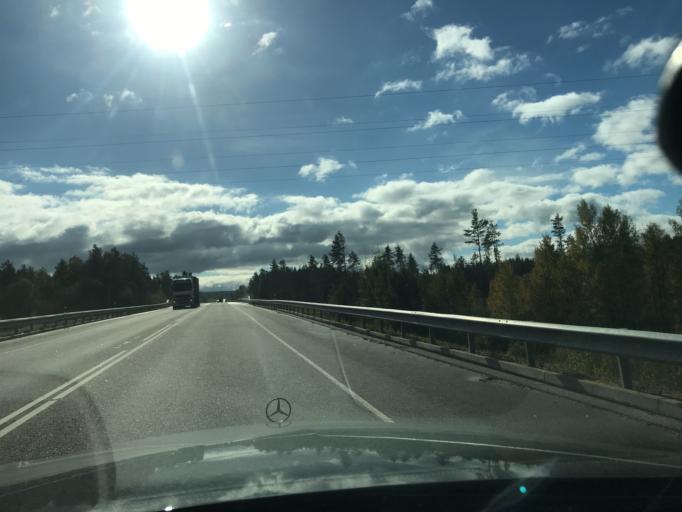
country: EE
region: Vorumaa
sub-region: Voru linn
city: Voru
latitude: 57.8269
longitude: 27.0634
